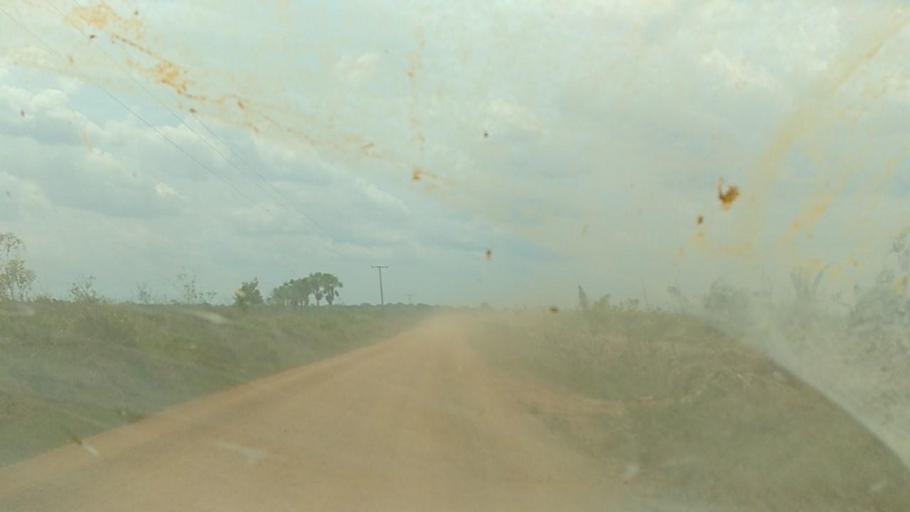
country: BR
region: Rondonia
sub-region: Porto Velho
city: Porto Velho
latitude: -8.9412
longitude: -64.3046
